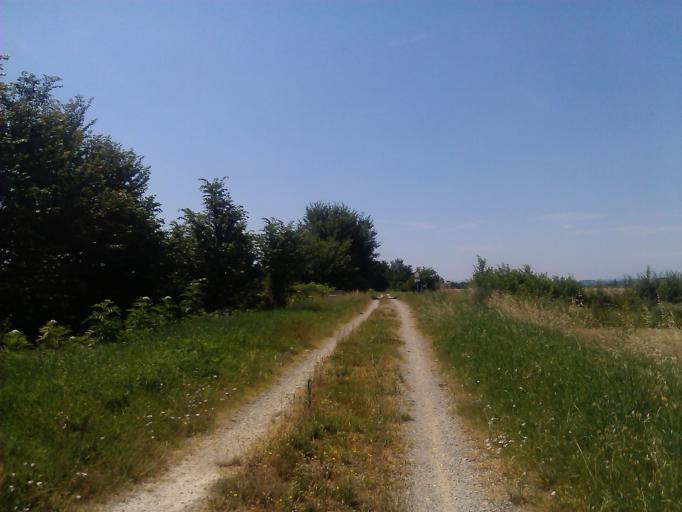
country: IT
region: Tuscany
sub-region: Province of Arezzo
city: Cesa
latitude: 43.3597
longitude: 11.8266
